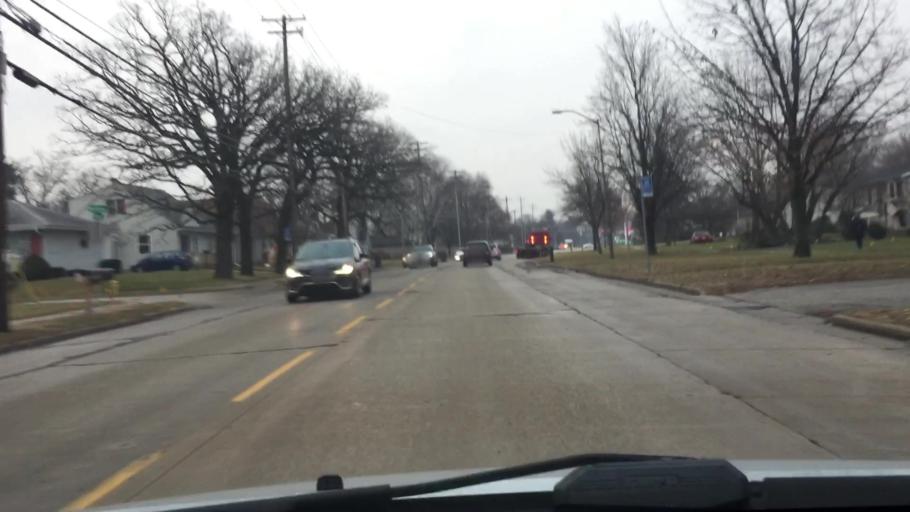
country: US
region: Wisconsin
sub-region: Waukesha County
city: Waukesha
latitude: 43.0219
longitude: -88.2591
